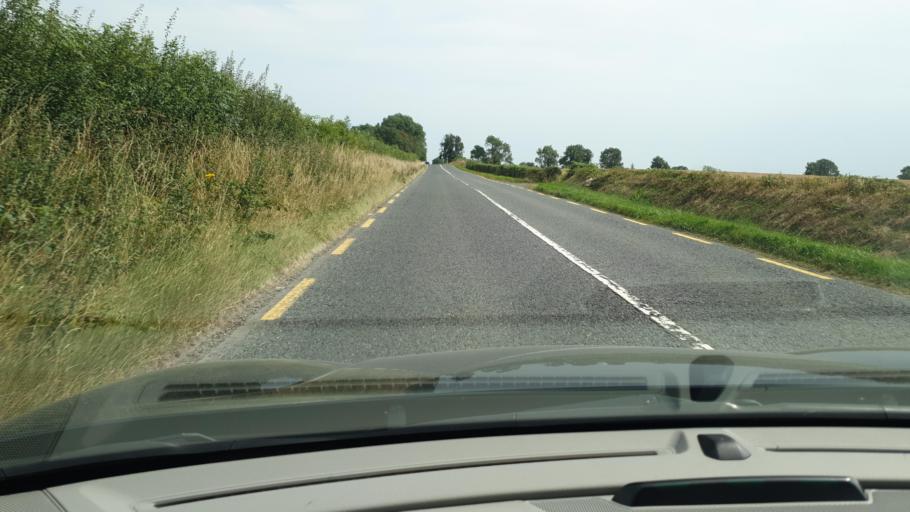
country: IE
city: Kentstown
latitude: 53.6345
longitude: -6.5874
